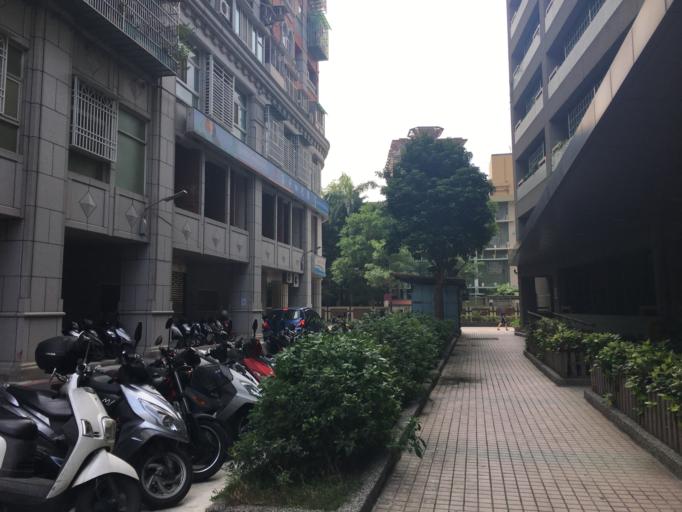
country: TW
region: Taipei
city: Taipei
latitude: 25.0859
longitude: 121.4775
